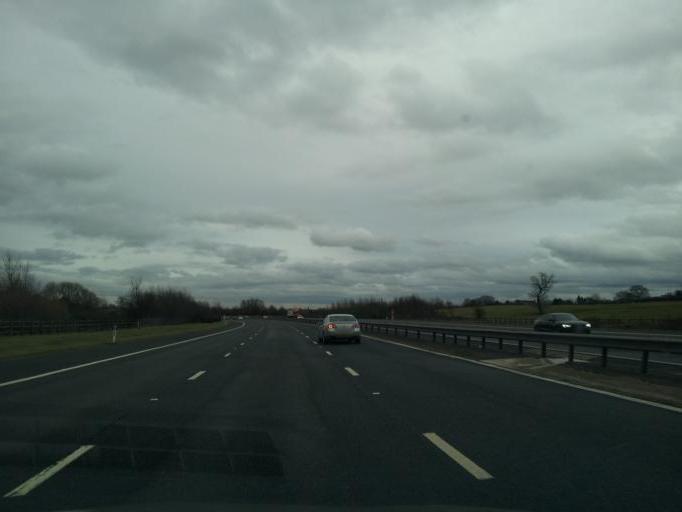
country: GB
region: England
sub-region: Staffordshire
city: Chasetown
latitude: 52.6539
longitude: -1.8991
